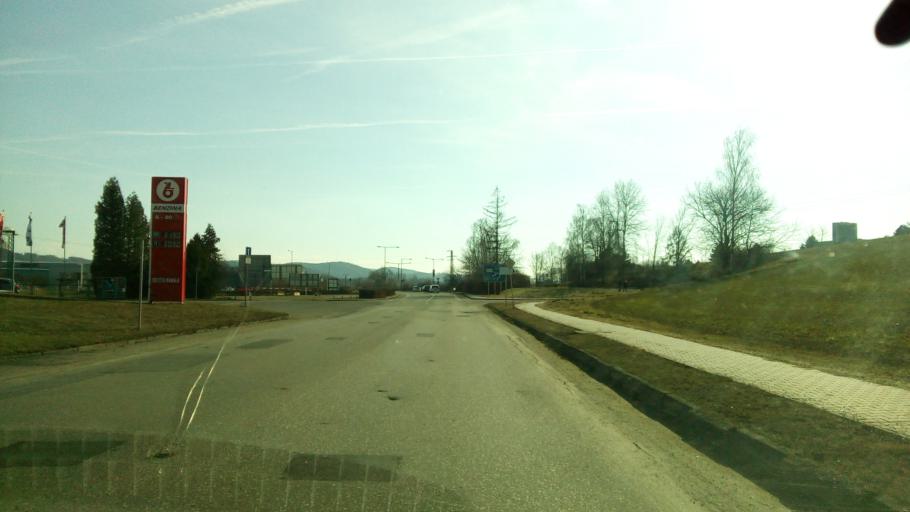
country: CZ
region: Olomoucky
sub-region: Okres Sumperk
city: Sumperk
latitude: 49.9542
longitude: 16.9607
